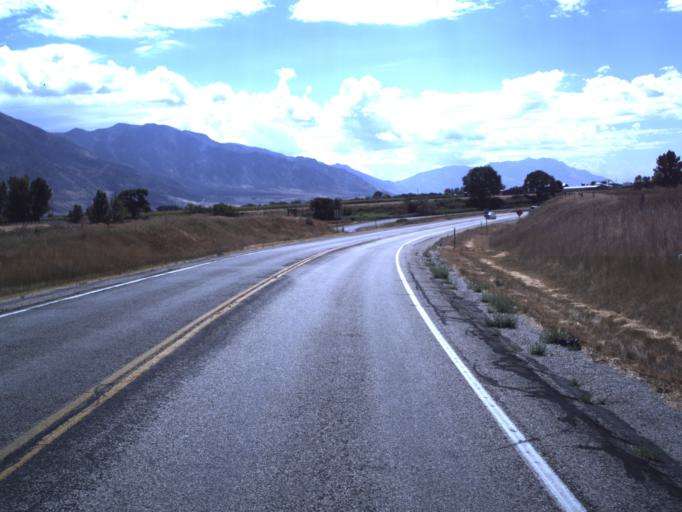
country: US
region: Utah
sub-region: Box Elder County
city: Garland
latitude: 41.7444
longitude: -112.1448
